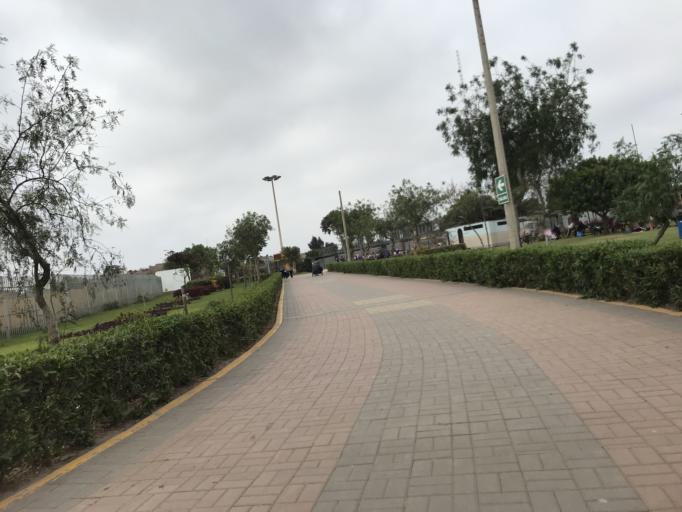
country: PE
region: Callao
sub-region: Callao
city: Callao
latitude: -12.0685
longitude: -77.0833
